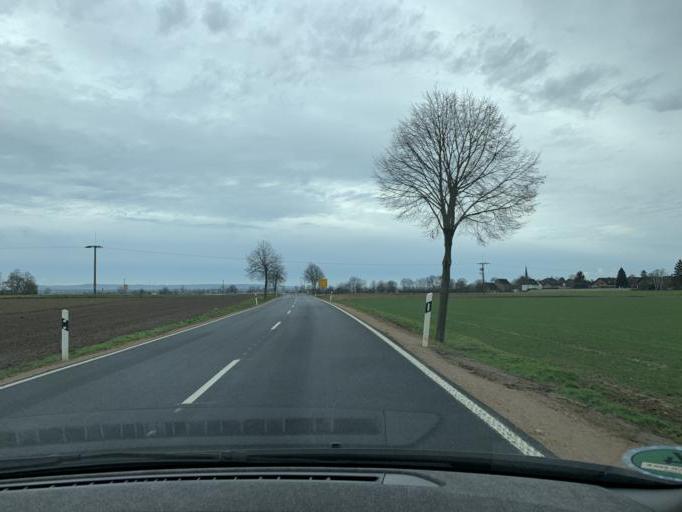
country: DE
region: North Rhine-Westphalia
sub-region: Regierungsbezirk Koln
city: Vettweiss
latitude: 50.7907
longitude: 6.5795
